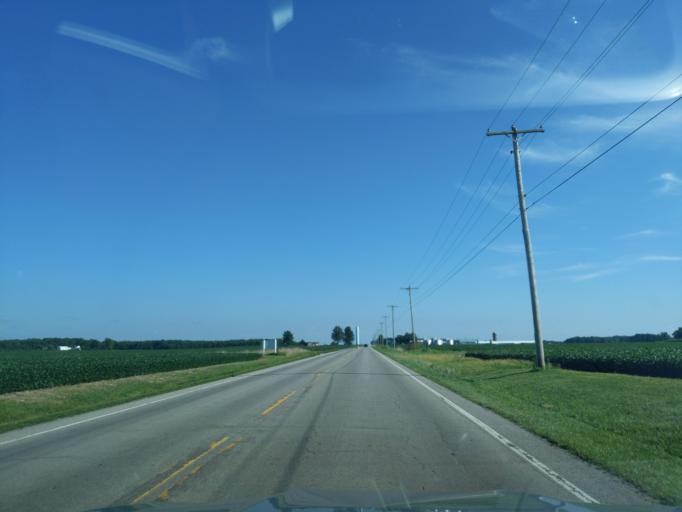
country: US
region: Indiana
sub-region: Ripley County
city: Osgood
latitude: 39.1921
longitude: -85.3240
